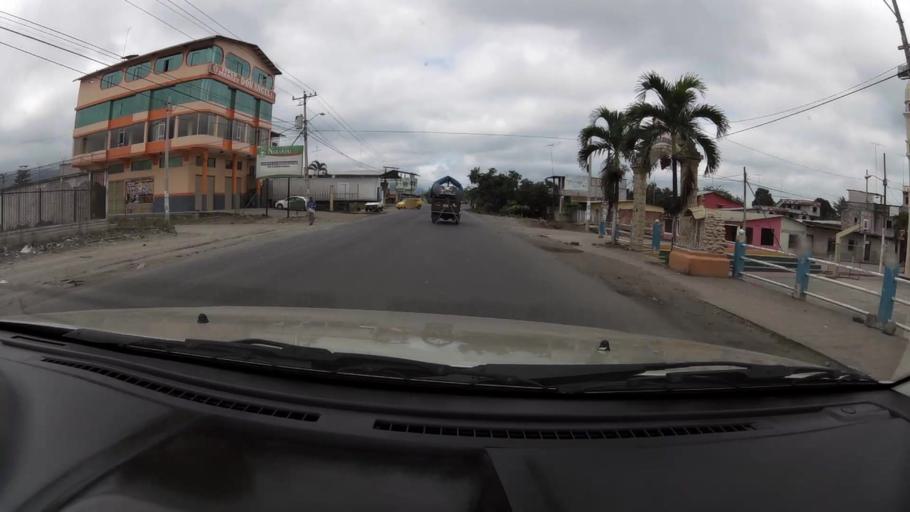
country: EC
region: Guayas
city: Naranjal
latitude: -2.6803
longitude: -79.6200
